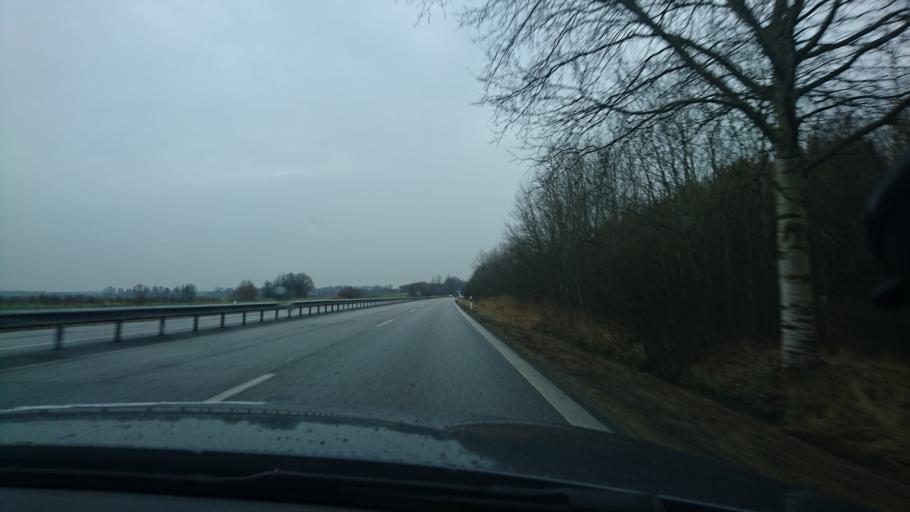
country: DE
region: Schleswig-Holstein
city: Altenkrempe
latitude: 54.1441
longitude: 10.8450
